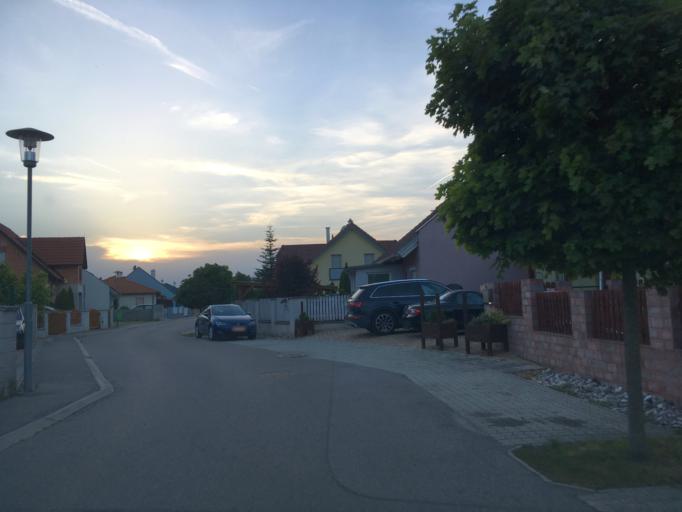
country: AT
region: Lower Austria
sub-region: Politischer Bezirk Baden
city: Teesdorf
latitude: 47.9466
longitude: 16.2828
